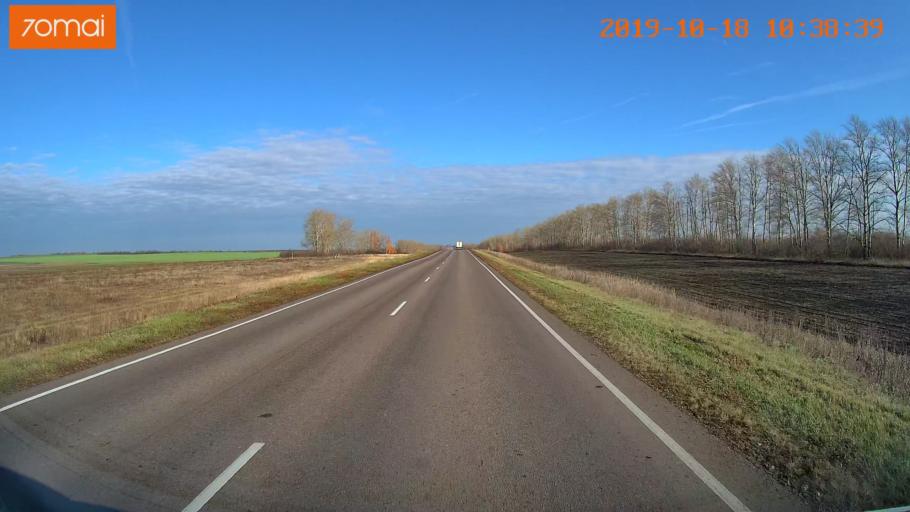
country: RU
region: Tula
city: Kurkino
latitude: 53.5760
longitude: 38.6440
